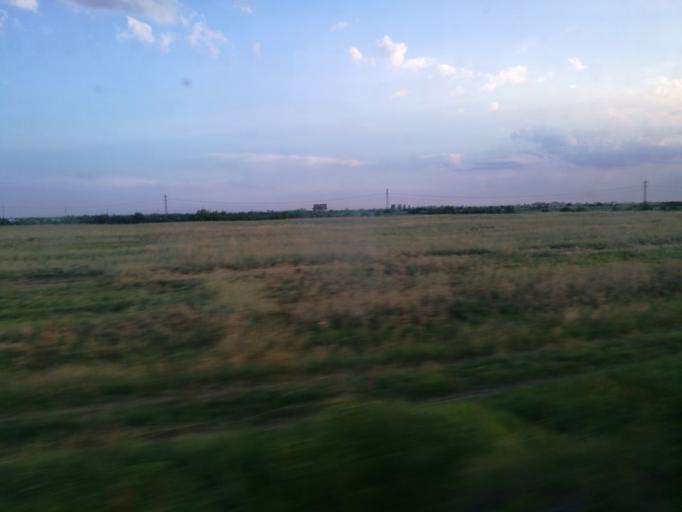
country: RO
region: Dambovita
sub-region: Comuna Racari
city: Mavrodin
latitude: 44.6447
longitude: 25.7084
